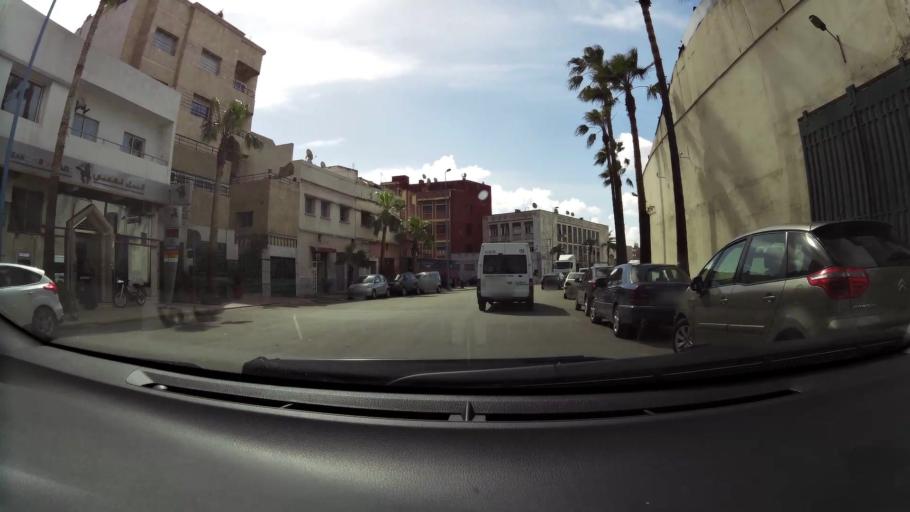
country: MA
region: Grand Casablanca
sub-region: Casablanca
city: Casablanca
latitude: 33.5874
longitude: -7.5761
